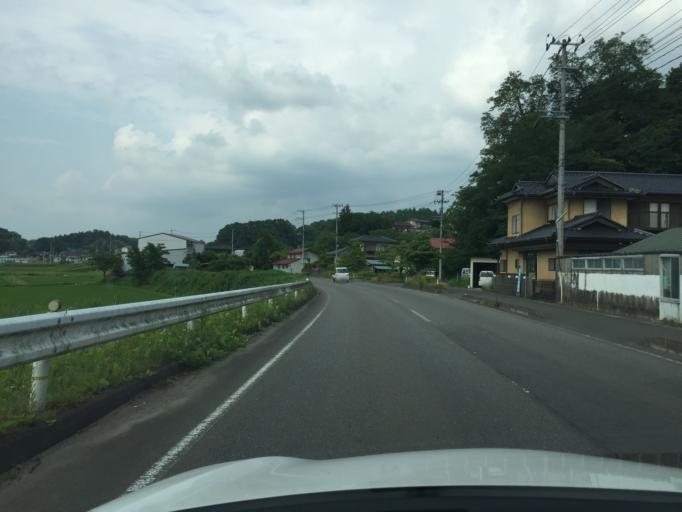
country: JP
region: Fukushima
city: Sukagawa
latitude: 37.2675
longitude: 140.4179
